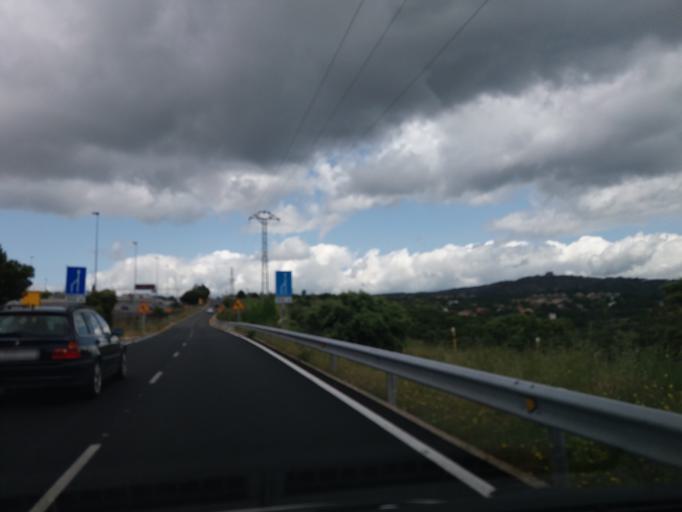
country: ES
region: Madrid
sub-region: Provincia de Madrid
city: Torrelodones
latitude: 40.5666
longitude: -3.9121
